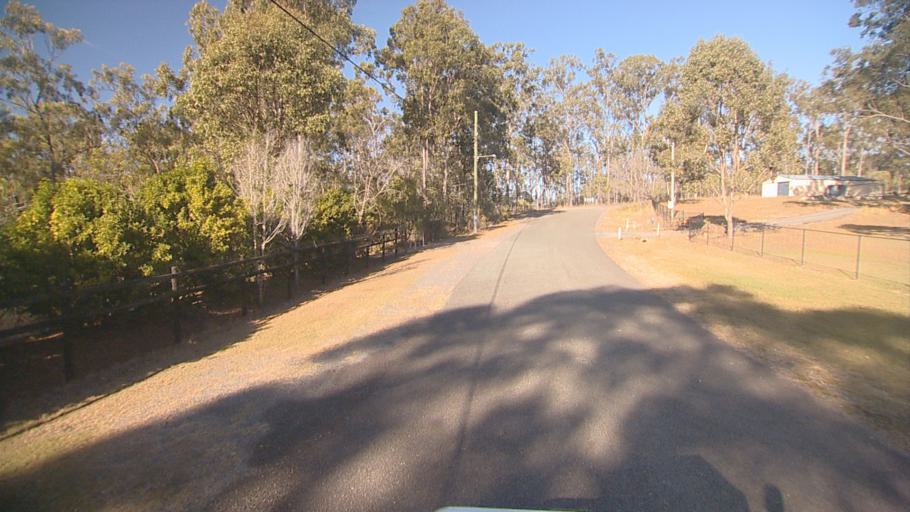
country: AU
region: Queensland
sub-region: Ipswich
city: Springfield Lakes
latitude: -27.7064
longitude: 152.9253
